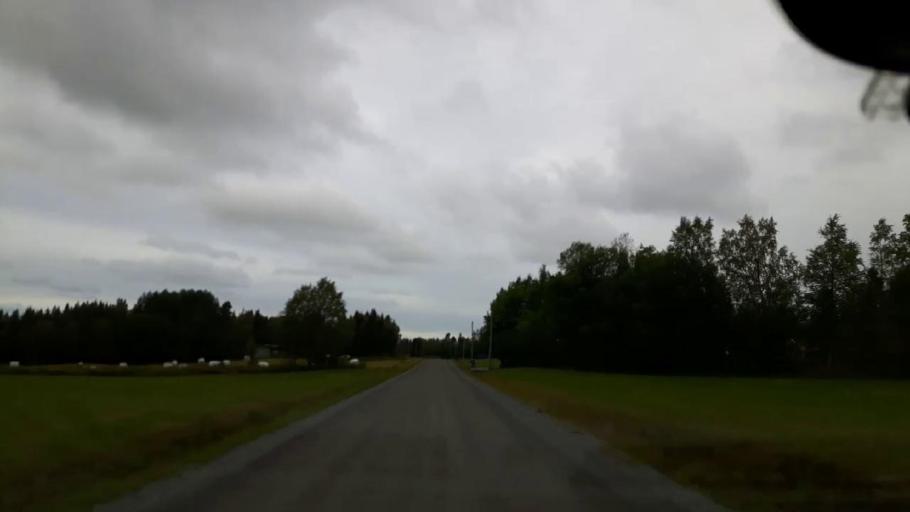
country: SE
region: Jaemtland
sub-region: OEstersunds Kommun
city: Ostersund
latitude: 63.0912
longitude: 14.5543
